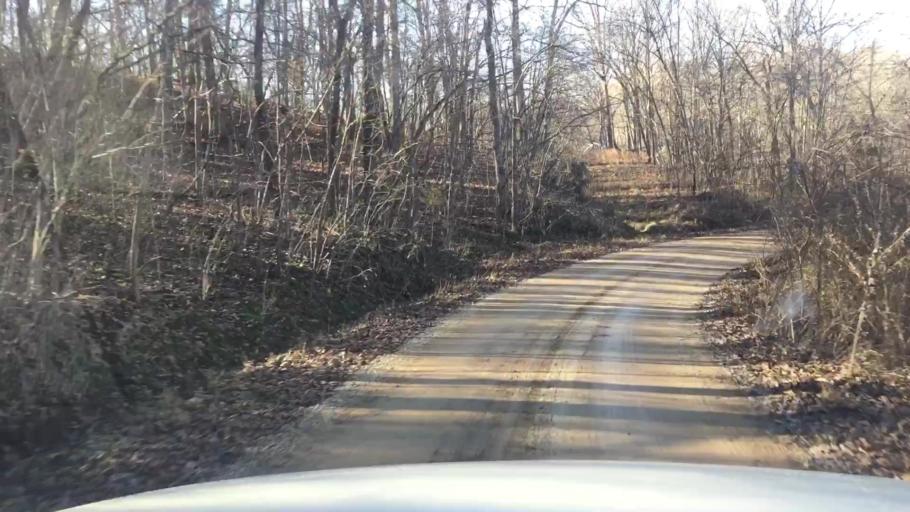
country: US
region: Missouri
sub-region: Morgan County
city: Versailles
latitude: 38.3248
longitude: -92.7690
